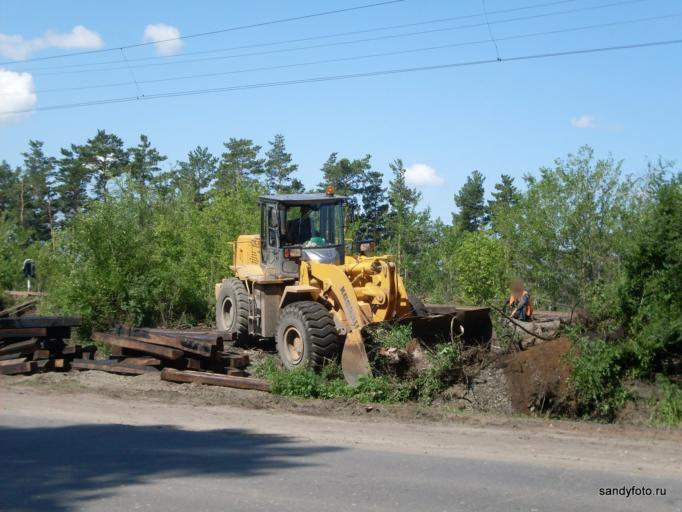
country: RU
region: Chelyabinsk
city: Troitsk
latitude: 54.0514
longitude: 61.6180
